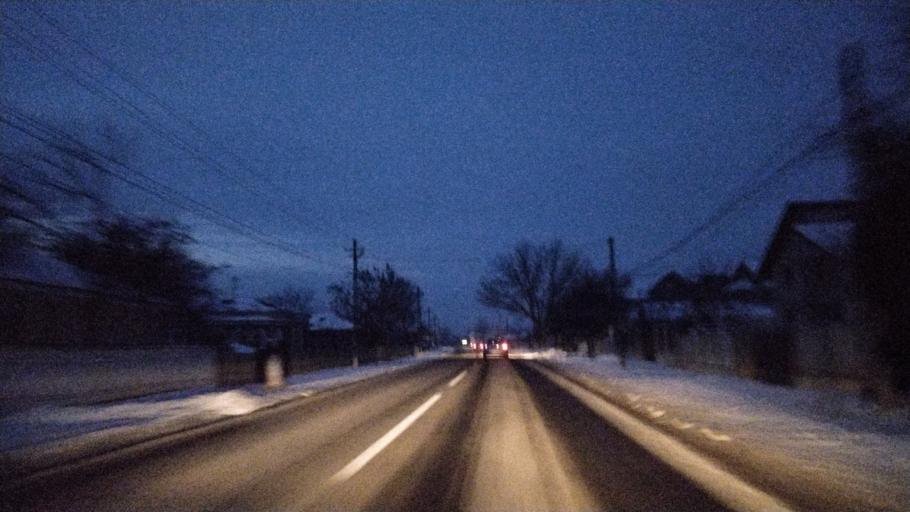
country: RO
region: Vrancea
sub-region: Comuna Rastoaca
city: Rastoaca
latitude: 45.6604
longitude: 27.2816
